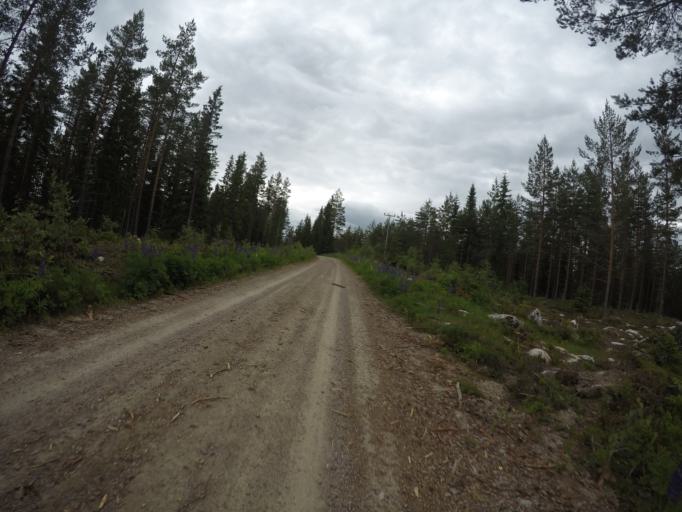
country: SE
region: Dalarna
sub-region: Ludvika Kommun
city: Abborrberget
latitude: 60.0944
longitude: 14.5468
